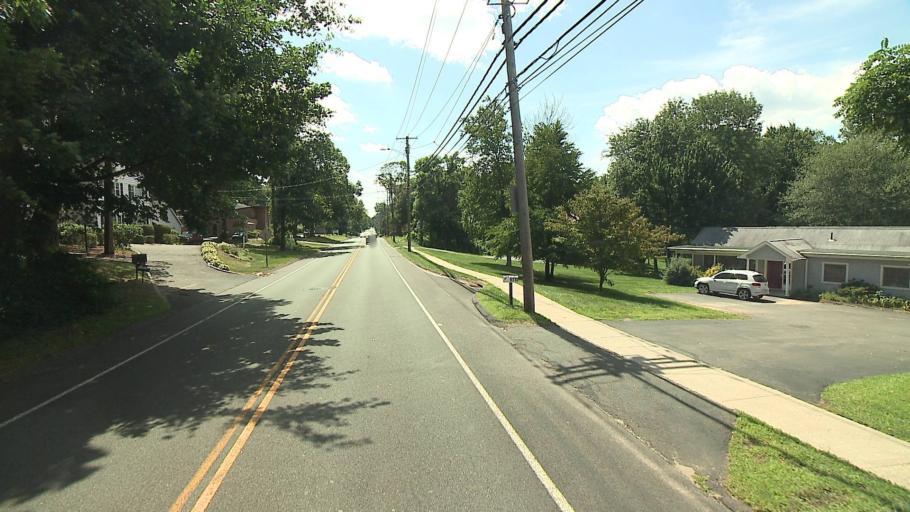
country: US
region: Connecticut
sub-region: Fairfield County
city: Trumbull
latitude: 41.2520
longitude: -73.2199
